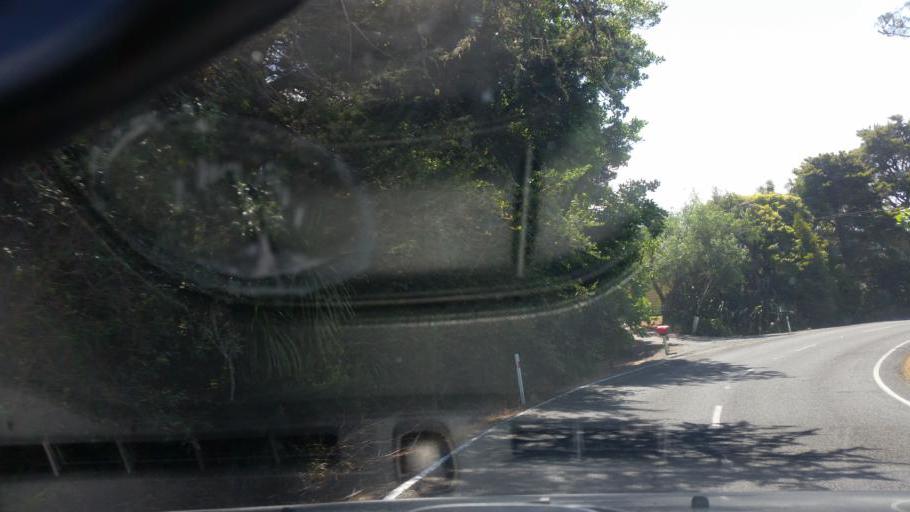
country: NZ
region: Northland
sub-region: Whangarei
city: Ruakaka
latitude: -36.1388
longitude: 174.2250
